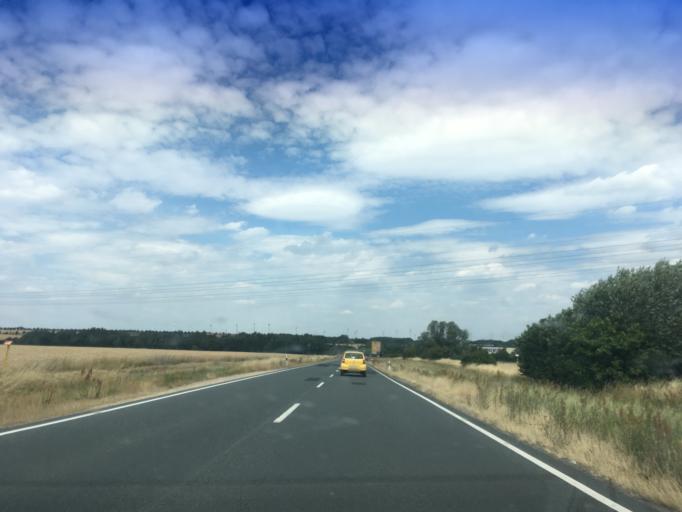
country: DE
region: Saxony
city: Goerlitz
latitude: 51.1672
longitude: 14.9582
